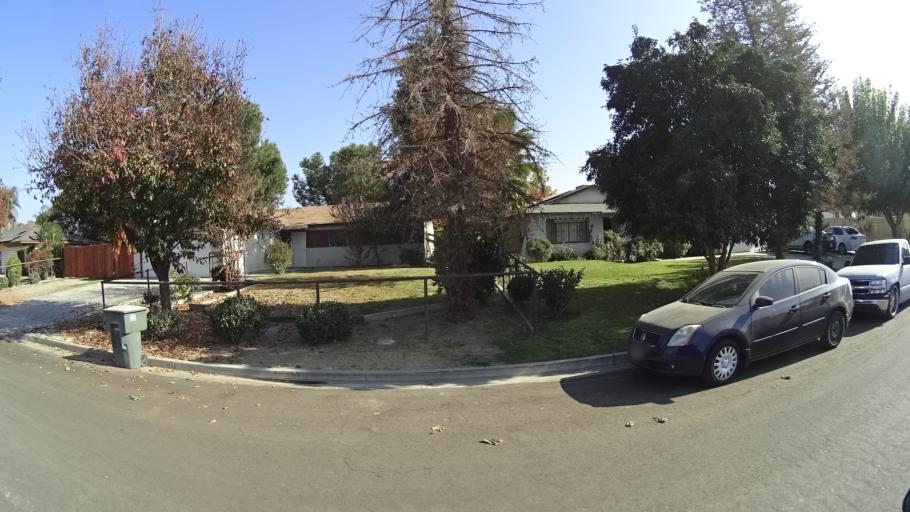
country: US
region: California
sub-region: Kern County
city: Greenfield
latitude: 35.2754
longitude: -119.0155
